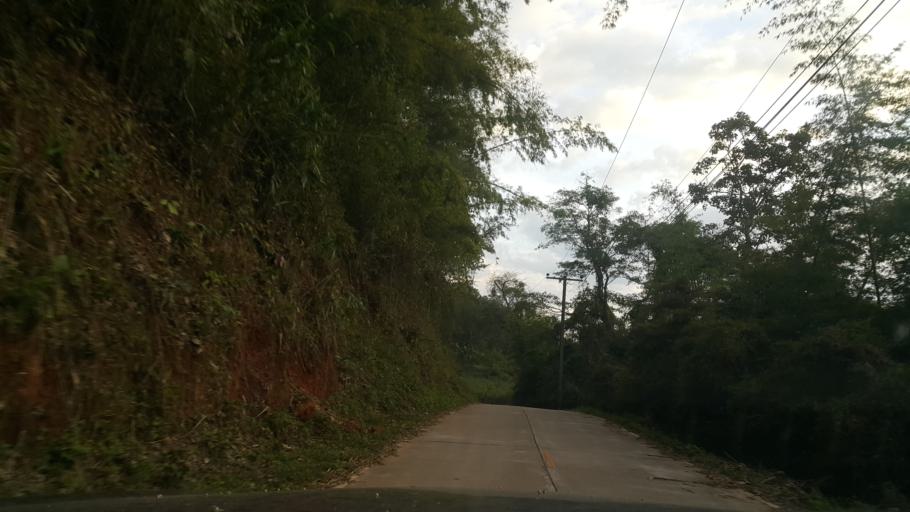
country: TH
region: Chiang Mai
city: Samoeng
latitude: 19.0009
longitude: 98.6737
